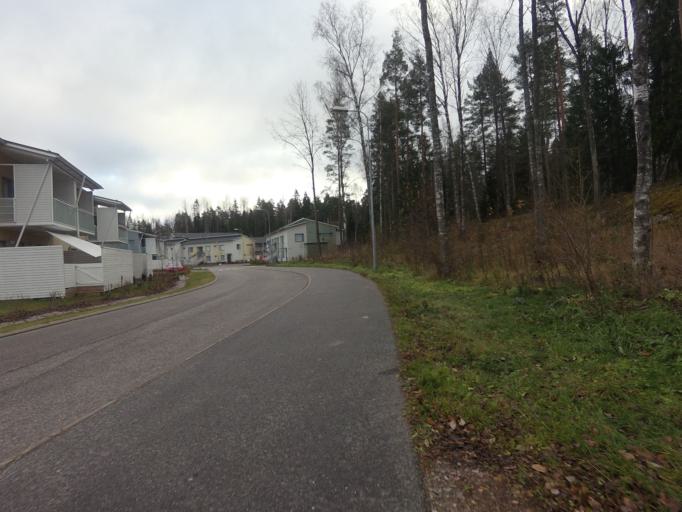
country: FI
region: Uusimaa
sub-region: Helsinki
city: Kauniainen
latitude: 60.1983
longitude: 24.7025
